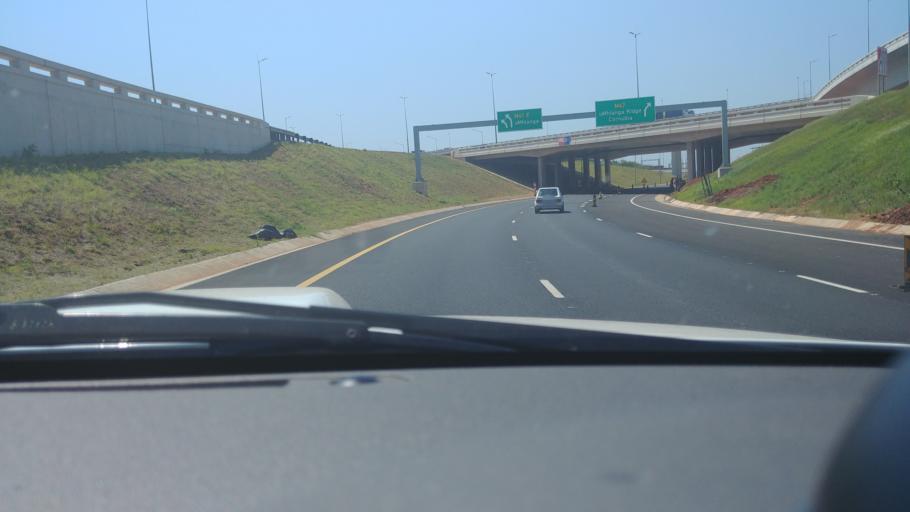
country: ZA
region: KwaZulu-Natal
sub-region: eThekwini Metropolitan Municipality
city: Durban
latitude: -29.7233
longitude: 31.0575
